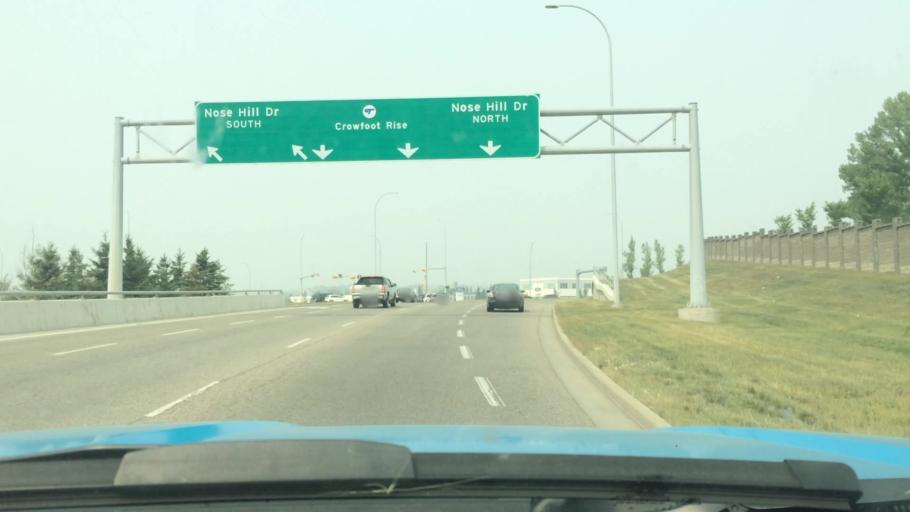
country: CA
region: Alberta
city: Calgary
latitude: 51.1201
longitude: -114.1998
